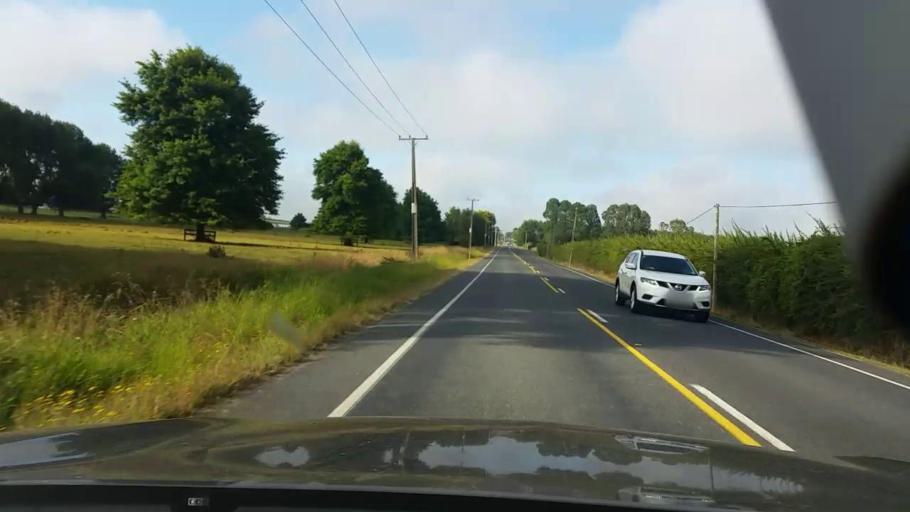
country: NZ
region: Waikato
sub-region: Hamilton City
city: Hamilton
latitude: -37.6020
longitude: 175.3518
